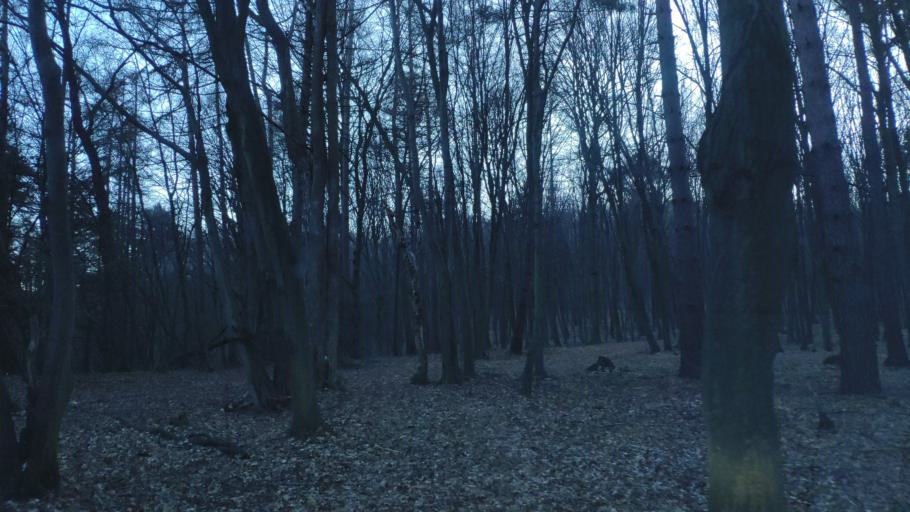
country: SK
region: Kosicky
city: Kosice
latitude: 48.8447
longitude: 21.2455
